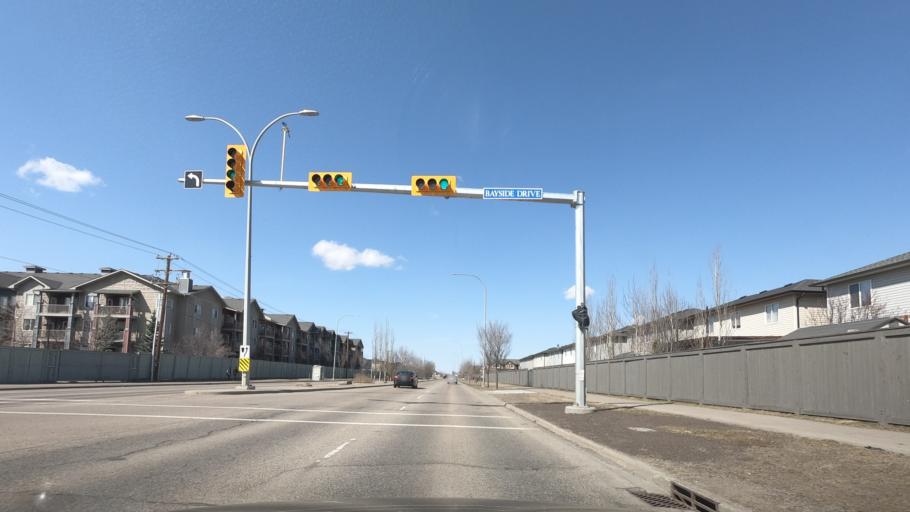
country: CA
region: Alberta
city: Airdrie
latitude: 51.2730
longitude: -114.0250
